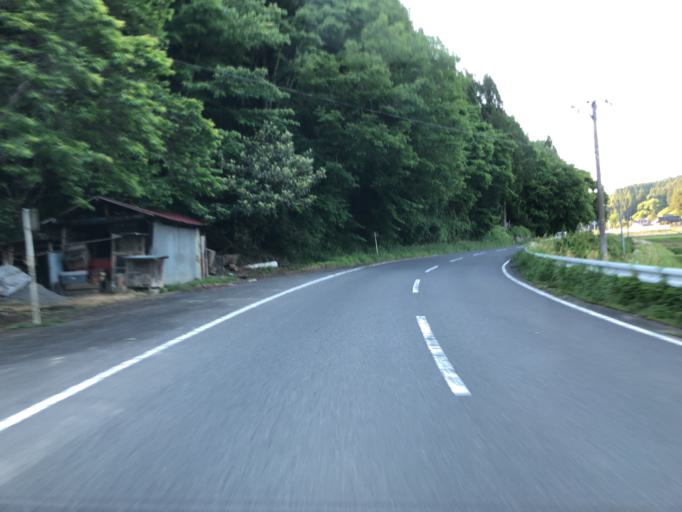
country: JP
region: Fukushima
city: Ishikawa
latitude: 36.9933
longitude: 140.4382
